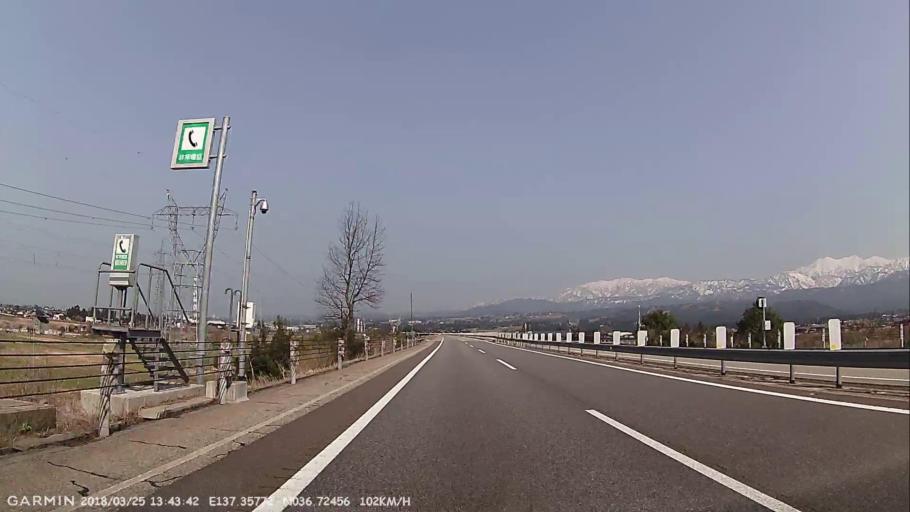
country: JP
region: Toyama
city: Kamiichi
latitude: 36.7263
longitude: 137.3579
